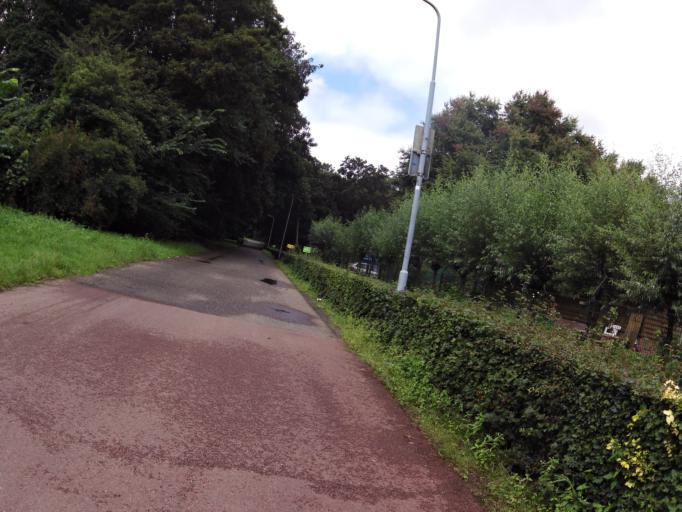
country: NL
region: Gelderland
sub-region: Gemeente Maasdriel
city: Hedel
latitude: 51.7000
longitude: 5.2557
